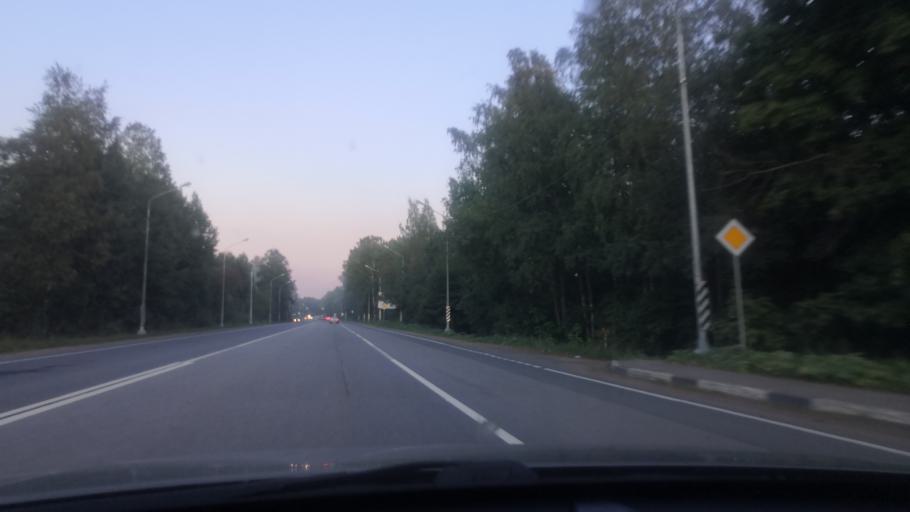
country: RU
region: St.-Petersburg
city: Beloostrov
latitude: 60.1961
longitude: 30.0502
